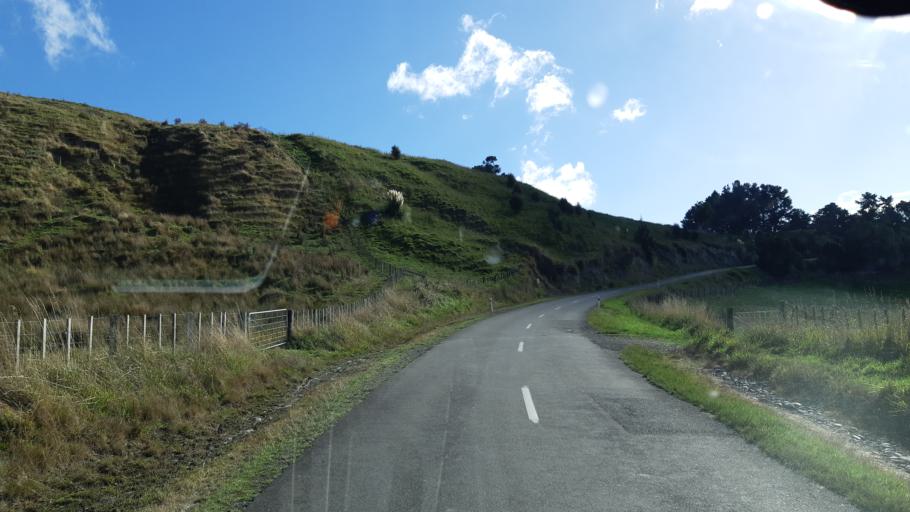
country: NZ
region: Manawatu-Wanganui
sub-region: Rangitikei District
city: Bulls
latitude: -39.9079
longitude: 175.3590
